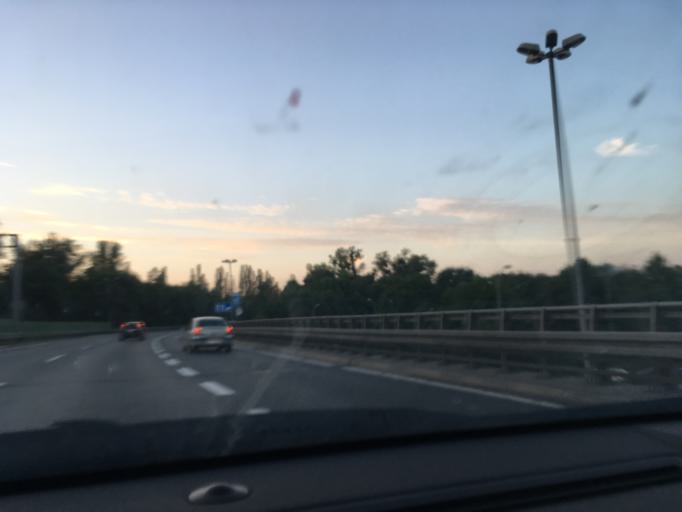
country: PL
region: Silesian Voivodeship
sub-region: Katowice
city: Katowice
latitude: 50.2619
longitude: 19.0465
